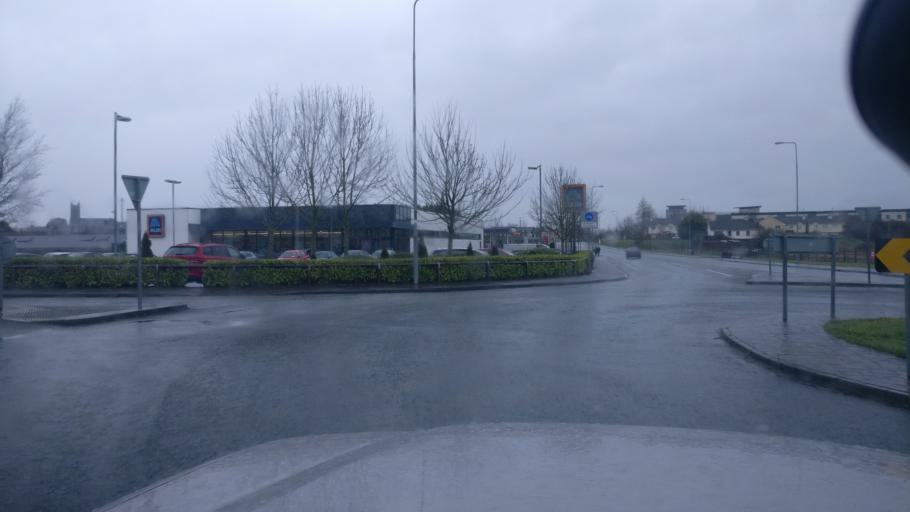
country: IE
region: Connaught
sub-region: County Galway
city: Ballinasloe
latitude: 53.3241
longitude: -8.2236
